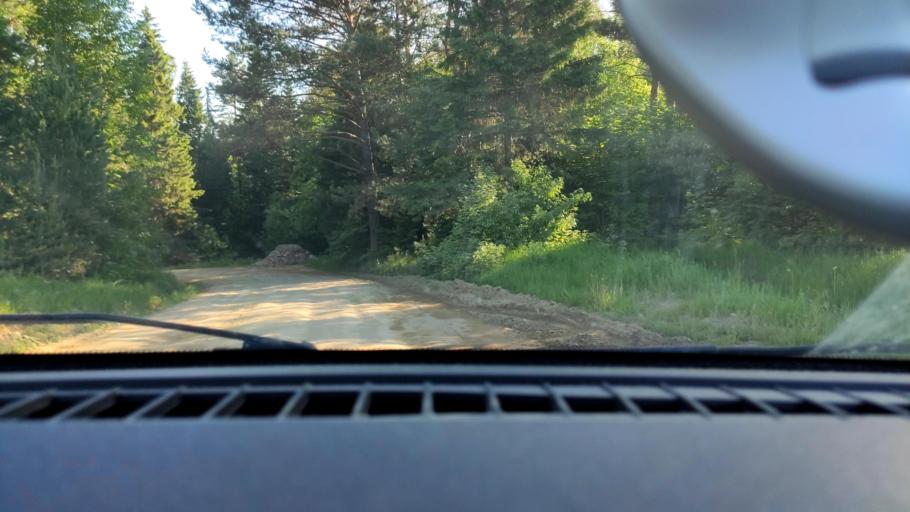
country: RU
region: Perm
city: Novyye Lyady
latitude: 58.1748
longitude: 56.5715
